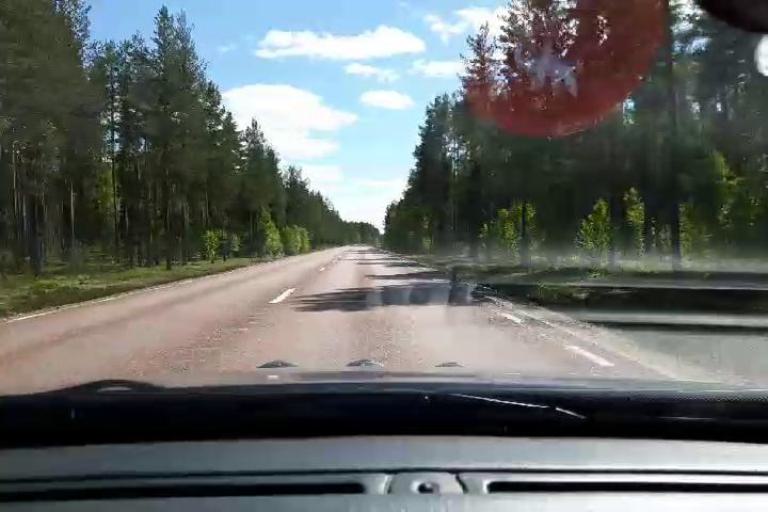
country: SE
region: Gaevleborg
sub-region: Ljusdals Kommun
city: Farila
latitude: 61.8275
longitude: 15.7538
